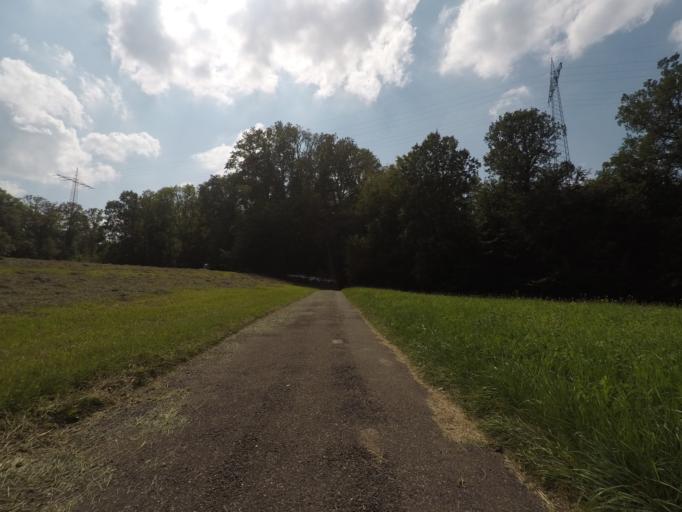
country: DE
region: Baden-Wuerttemberg
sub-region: Regierungsbezirk Stuttgart
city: Winterbach
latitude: 48.7874
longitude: 9.4612
